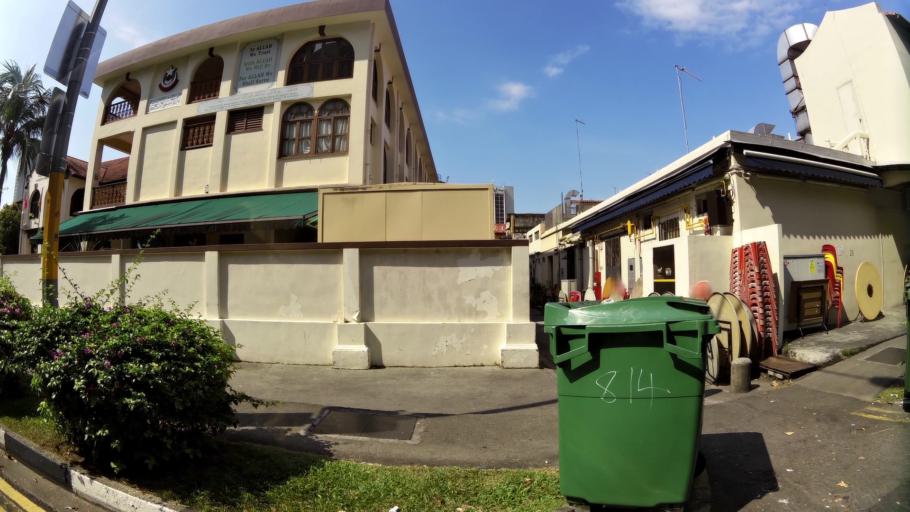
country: SG
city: Singapore
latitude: 1.3039
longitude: 103.8608
